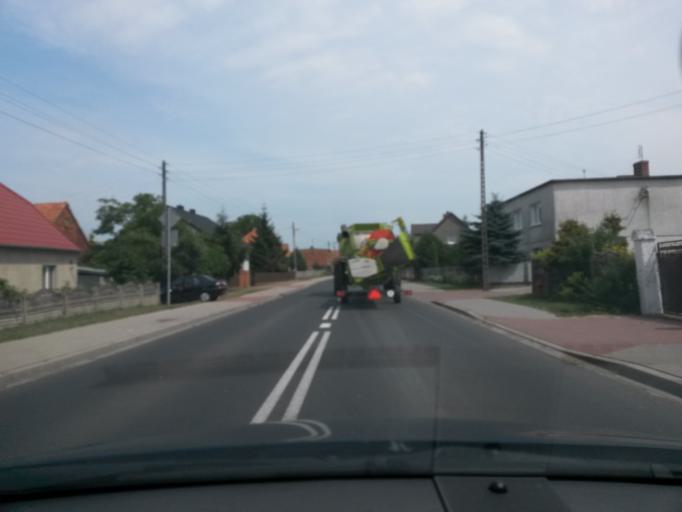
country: PL
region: Greater Poland Voivodeship
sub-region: Powiat sremski
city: Dolsk
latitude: 51.9487
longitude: 17.0539
